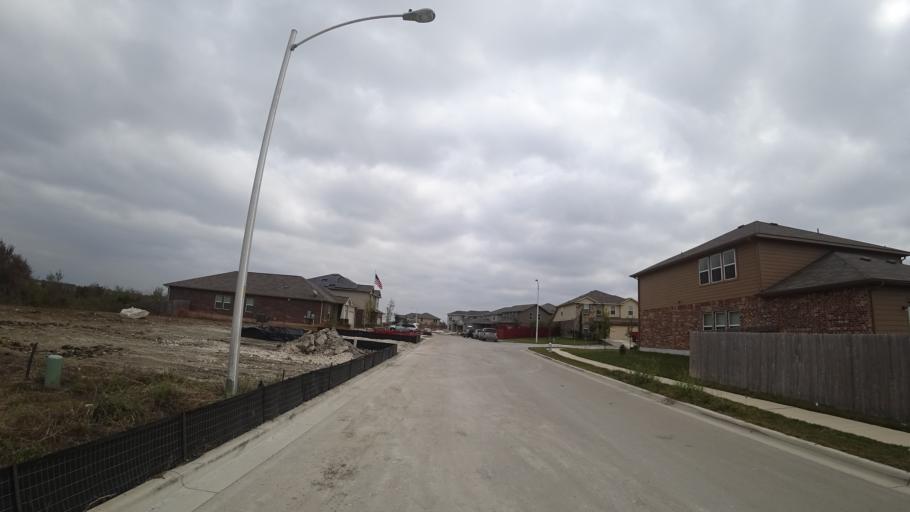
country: US
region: Texas
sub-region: Travis County
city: Pflugerville
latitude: 30.3948
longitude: -97.6202
